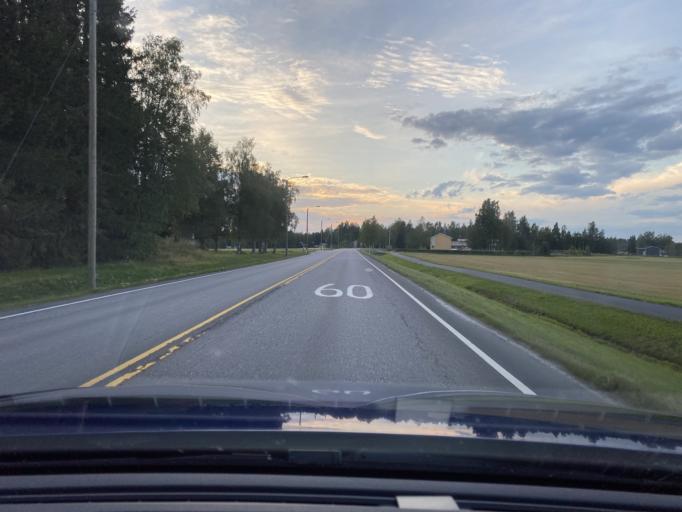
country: FI
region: Satakunta
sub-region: Pohjois-Satakunta
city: Kankaanpaeae
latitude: 61.7537
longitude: 22.5094
